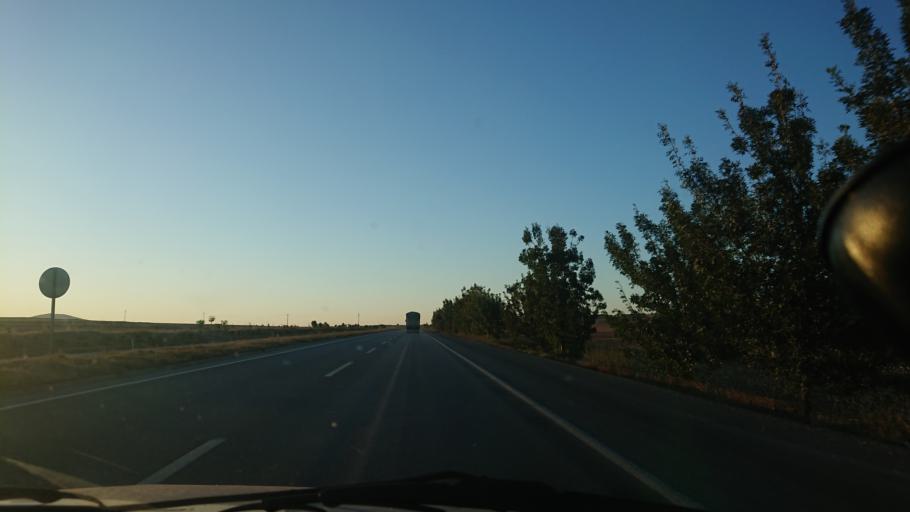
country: TR
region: Eskisehir
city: Mahmudiye
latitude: 39.4932
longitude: 30.9757
